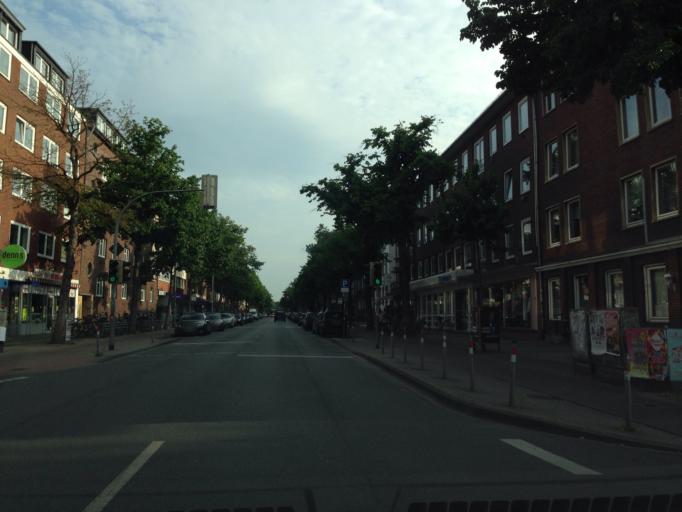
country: DE
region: North Rhine-Westphalia
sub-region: Regierungsbezirk Munster
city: Muenster
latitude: 51.9527
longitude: 7.6255
